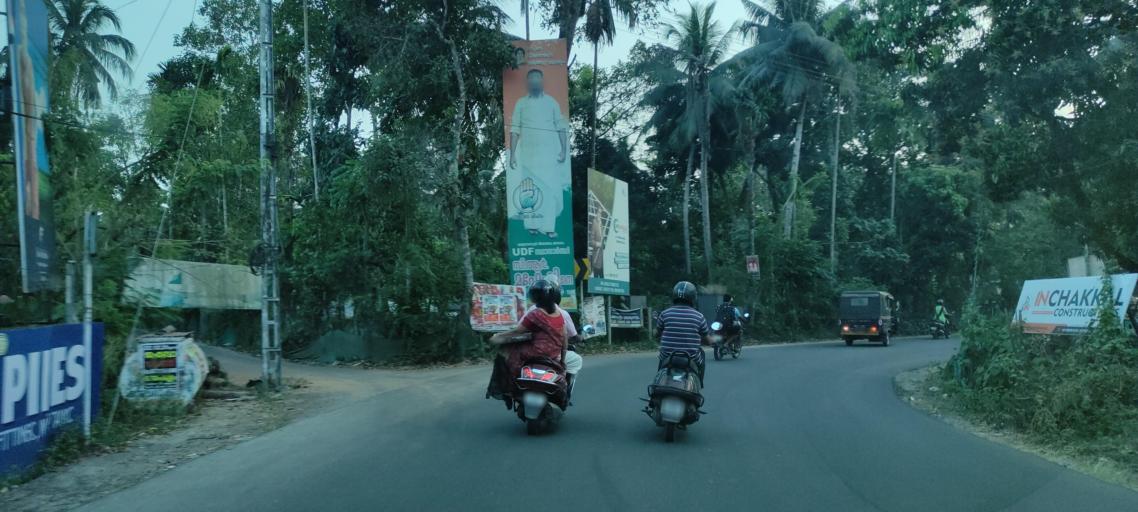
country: IN
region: Kerala
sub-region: Alappuzha
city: Kayankulam
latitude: 9.1312
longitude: 76.5058
